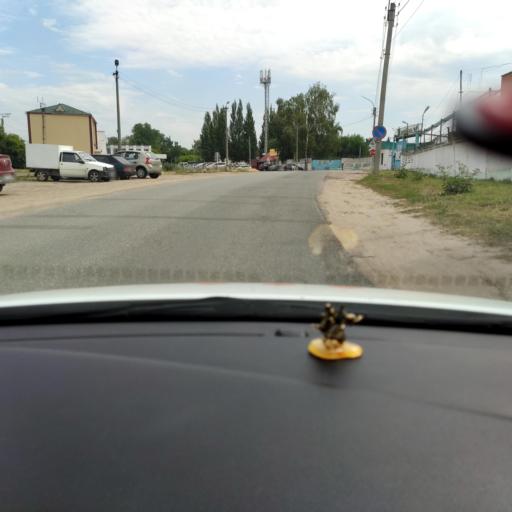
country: RU
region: Tatarstan
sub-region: Zelenodol'skiy Rayon
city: Zelenodolsk
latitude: 55.8413
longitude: 48.5580
